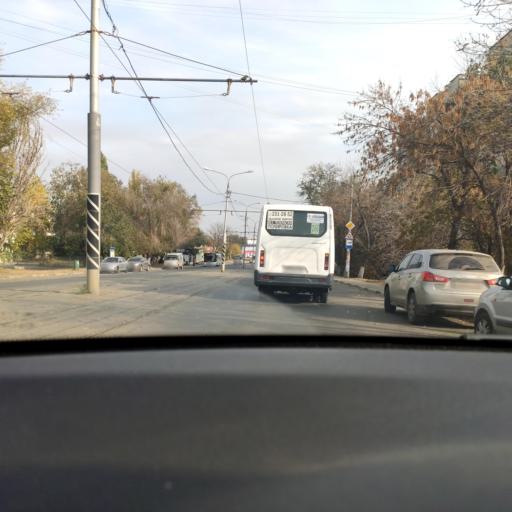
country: RU
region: Samara
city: Samara
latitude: 53.1922
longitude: 50.2099
